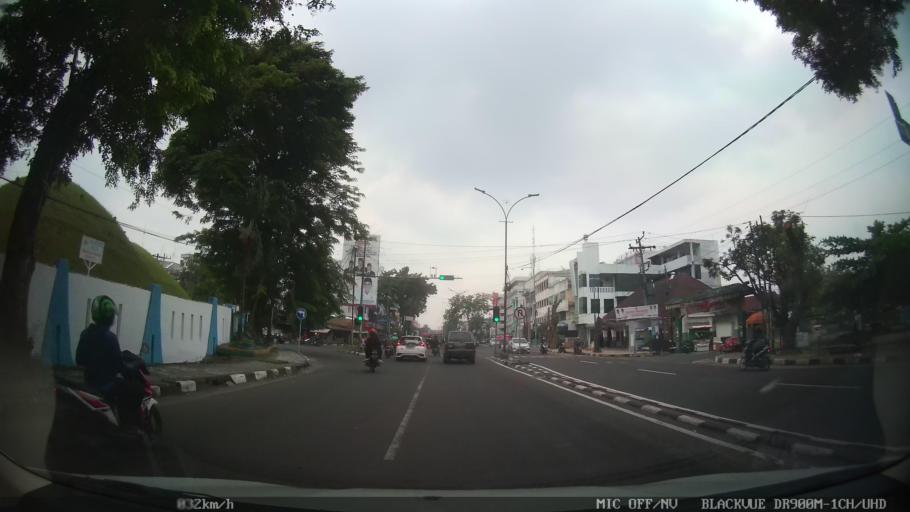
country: ID
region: North Sumatra
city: Medan
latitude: 3.5803
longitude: 98.6856
